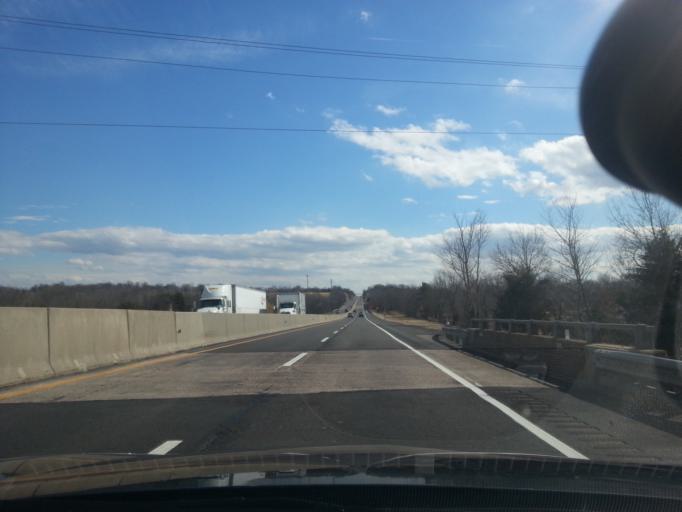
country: US
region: Pennsylvania
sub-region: Montgomery County
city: Harleysville
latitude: 40.3322
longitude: -75.3816
